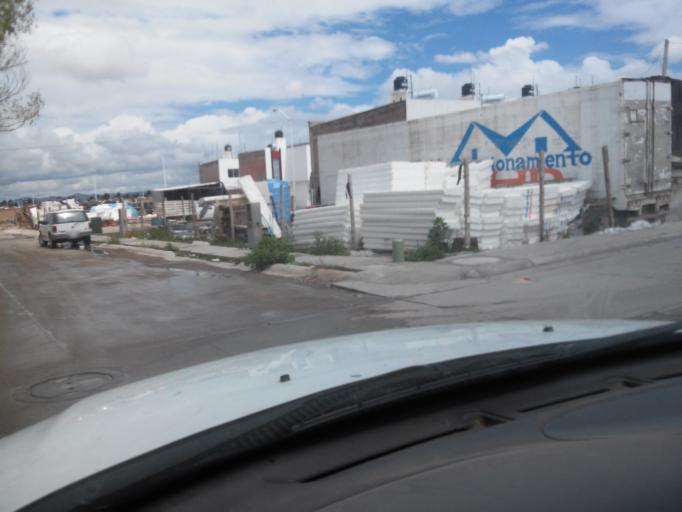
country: MX
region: Durango
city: Victoria de Durango
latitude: 24.0201
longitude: -104.6118
